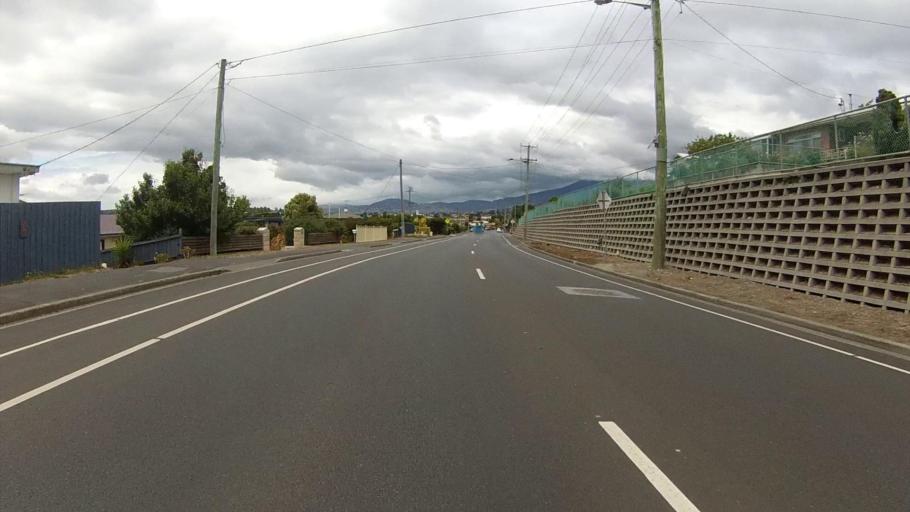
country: AU
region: Tasmania
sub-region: Glenorchy
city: Claremont
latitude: -42.7781
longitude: 147.2518
